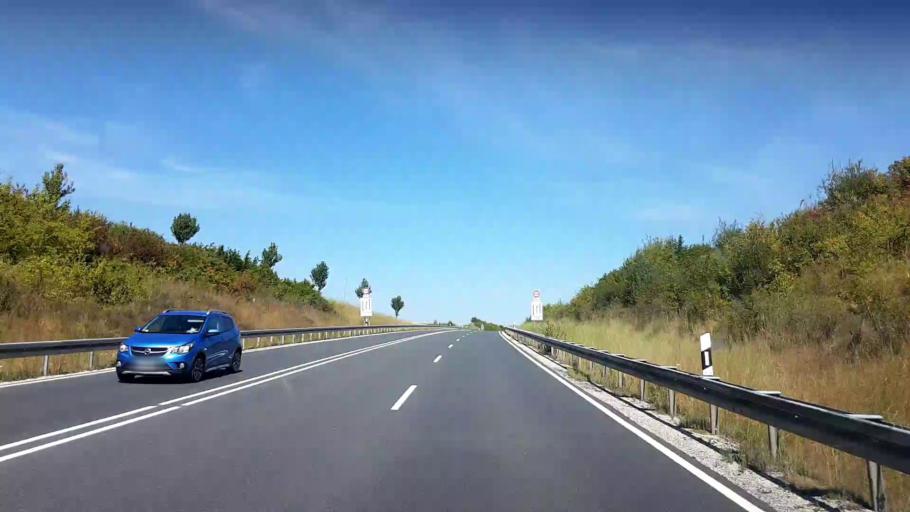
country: DE
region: Bavaria
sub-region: Upper Franconia
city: Untersiemau
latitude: 50.1693
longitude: 10.9931
